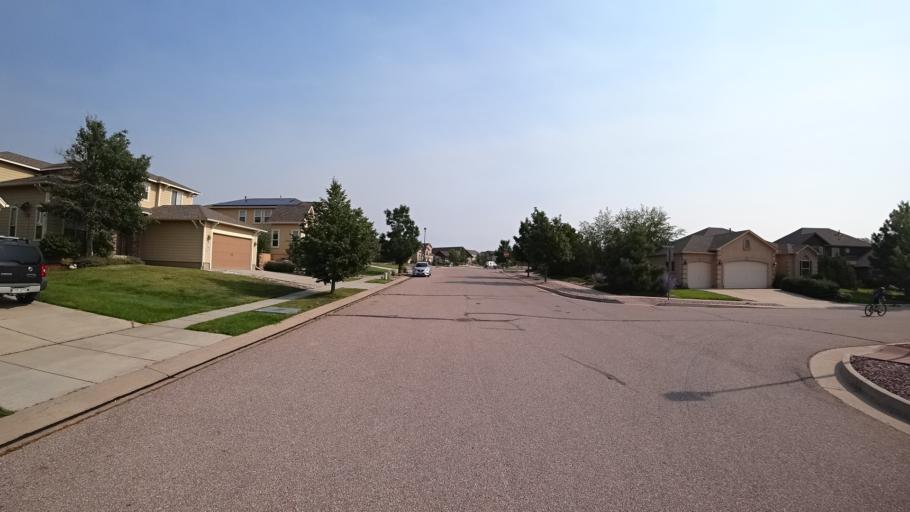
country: US
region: Colorado
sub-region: El Paso County
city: Black Forest
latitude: 38.9579
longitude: -104.7209
